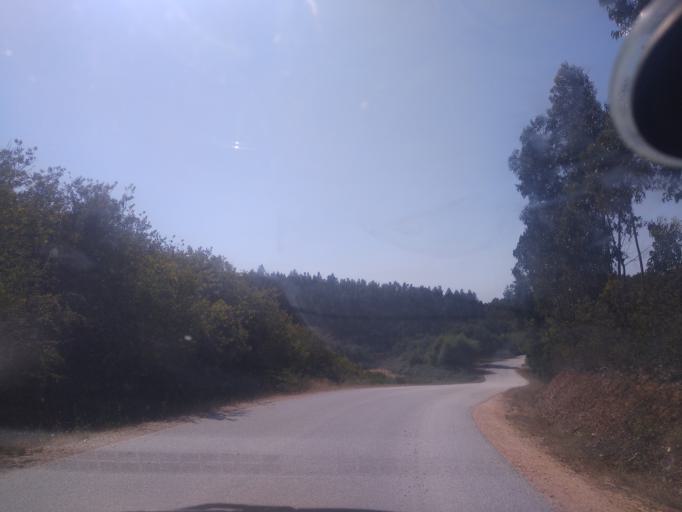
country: PT
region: Faro
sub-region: Aljezur
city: Aljezur
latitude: 37.2205
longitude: -8.8007
